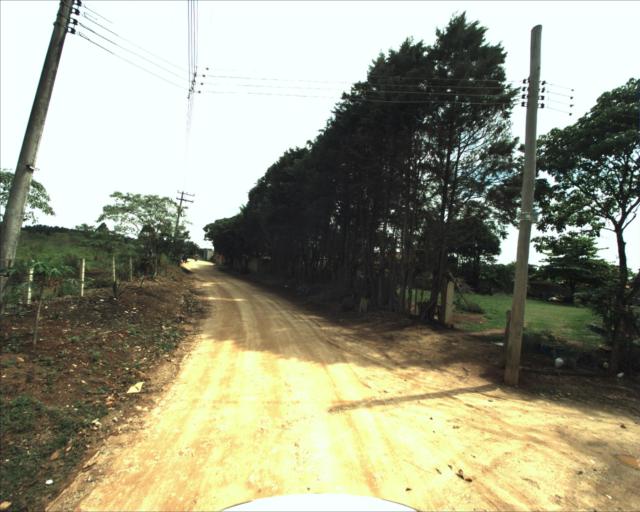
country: BR
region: Sao Paulo
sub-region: Aracoiaba Da Serra
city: Aracoiaba da Serra
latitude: -23.5590
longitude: -47.5556
